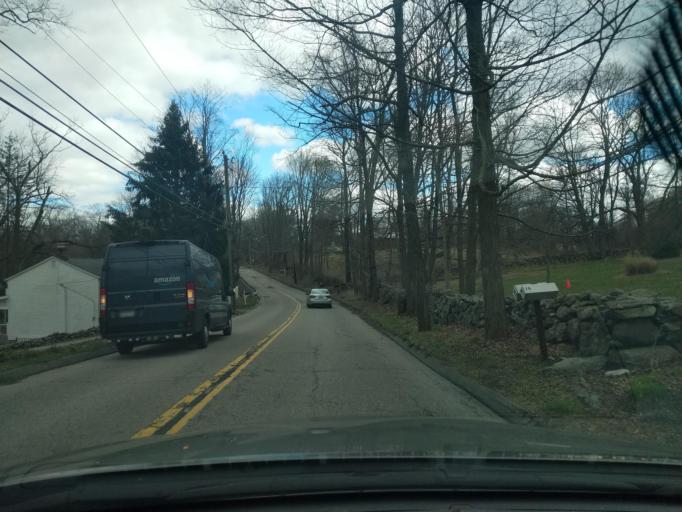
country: US
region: Connecticut
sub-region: Fairfield County
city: Newtown
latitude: 41.3651
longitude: -73.3291
